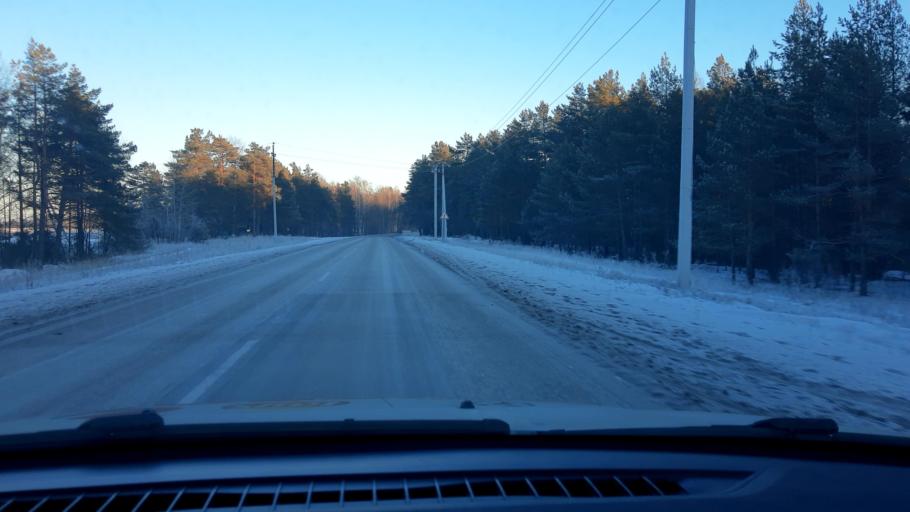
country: RU
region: Nizjnij Novgorod
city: Novosmolinskiy
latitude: 56.3199
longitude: 43.0106
